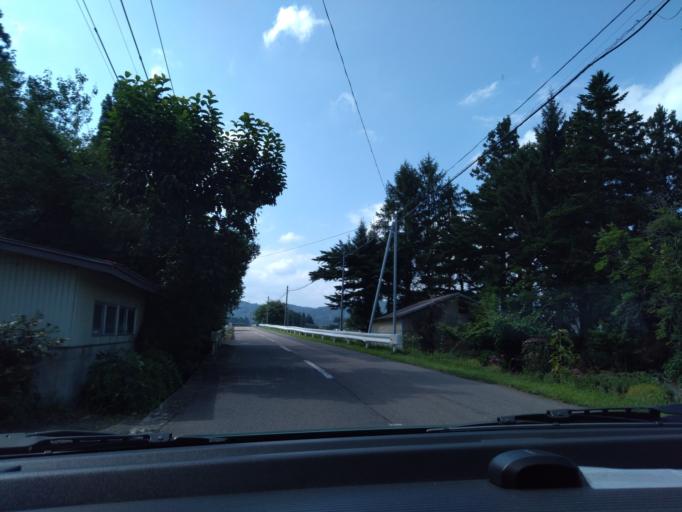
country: JP
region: Iwate
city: Shizukuishi
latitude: 39.6854
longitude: 140.9521
